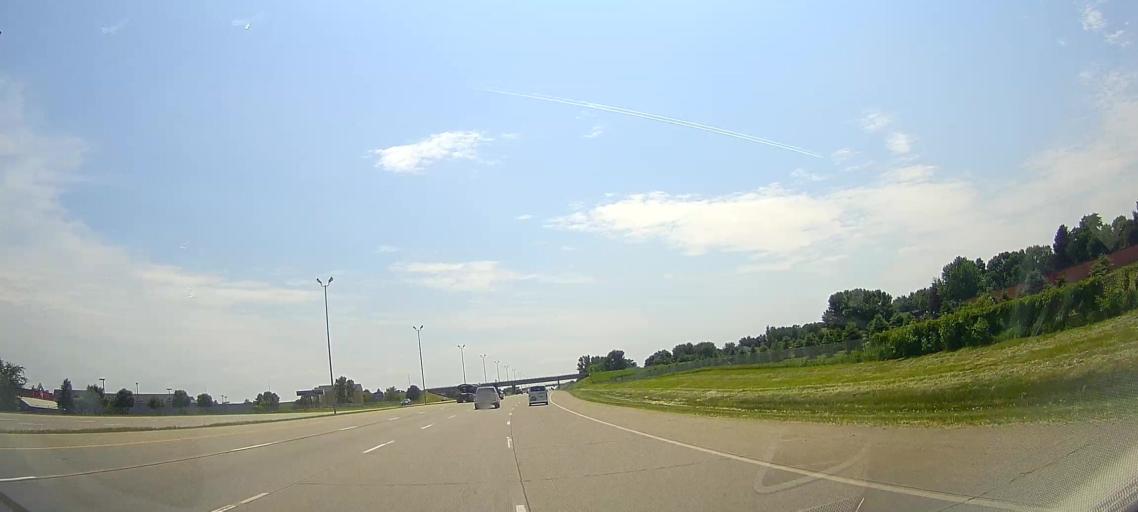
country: US
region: South Dakota
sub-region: Lincoln County
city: Tea
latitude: 43.5105
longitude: -96.7818
